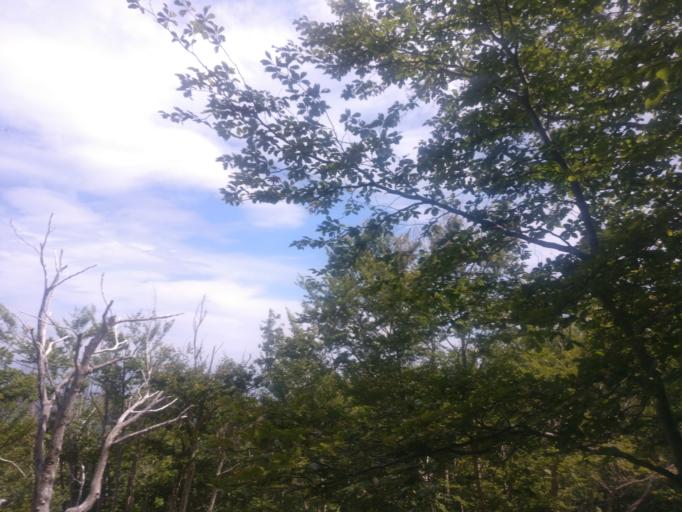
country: ME
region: Kotor
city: Kotor
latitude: 42.4056
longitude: 18.8398
